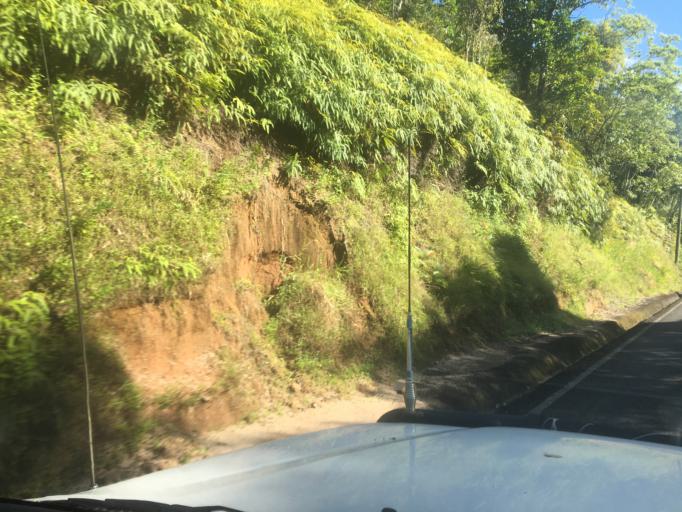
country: AU
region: Queensland
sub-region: Cassowary Coast
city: Innisfail
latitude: -17.3453
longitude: 145.8745
